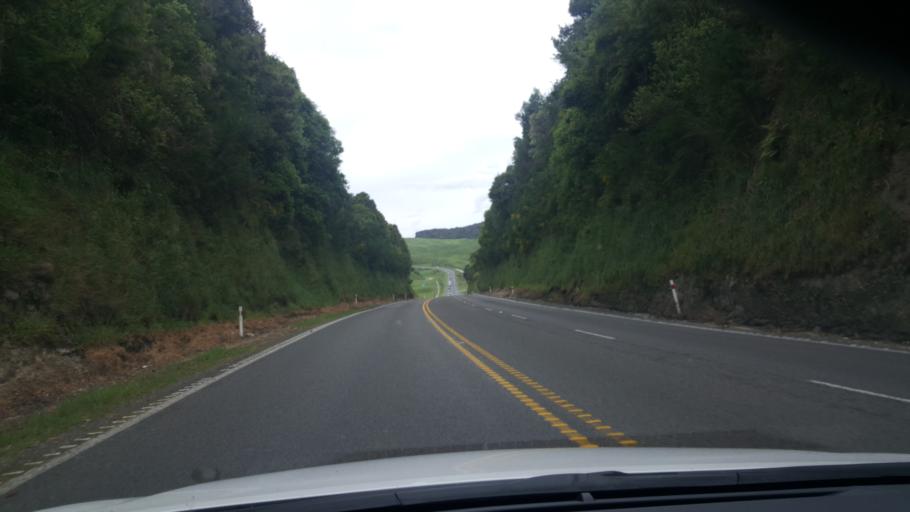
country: NZ
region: Bay of Plenty
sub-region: Rotorua District
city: Rotorua
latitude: -38.2503
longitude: 176.3179
